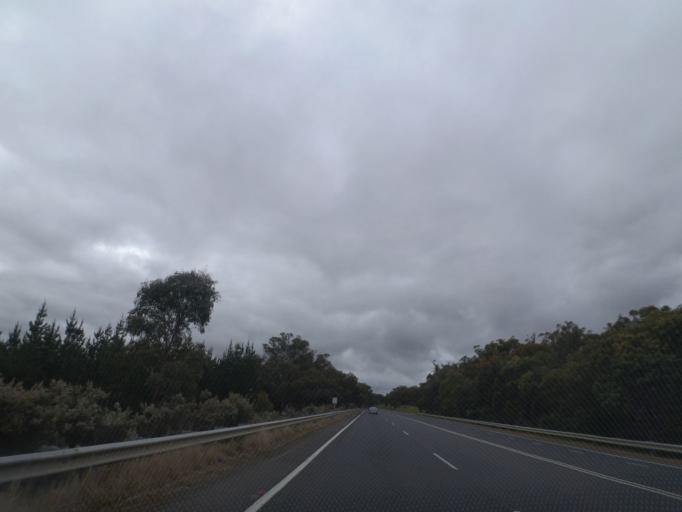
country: AU
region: Victoria
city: Black Hill
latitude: -37.4517
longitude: 143.8755
